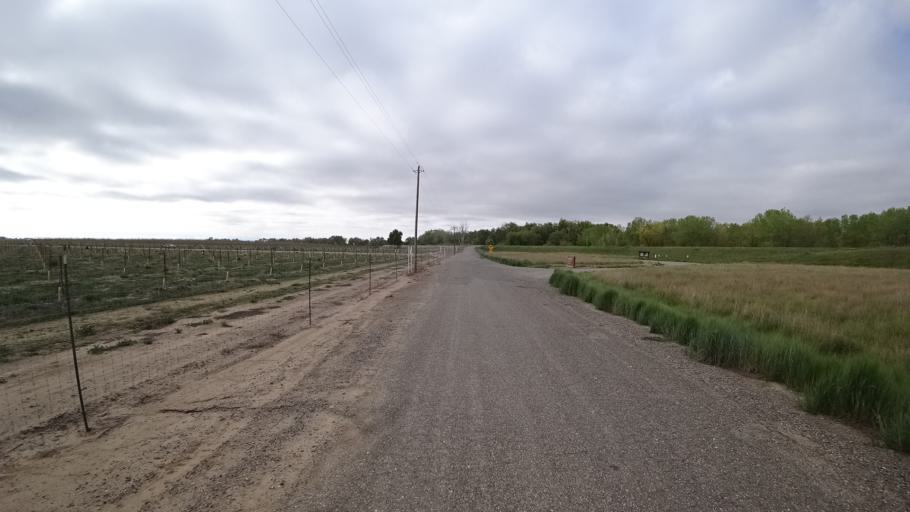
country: US
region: California
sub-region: Colusa County
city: Colusa
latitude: 39.4163
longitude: -121.9921
